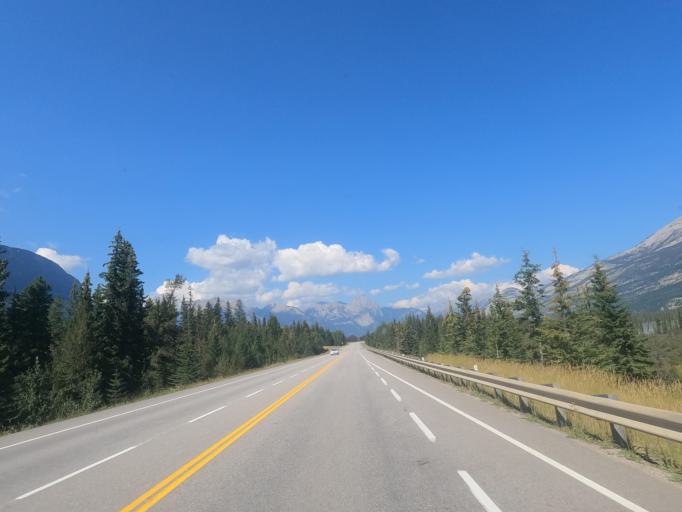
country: CA
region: Alberta
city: Jasper Park Lodge
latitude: 52.9641
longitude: -118.0521
